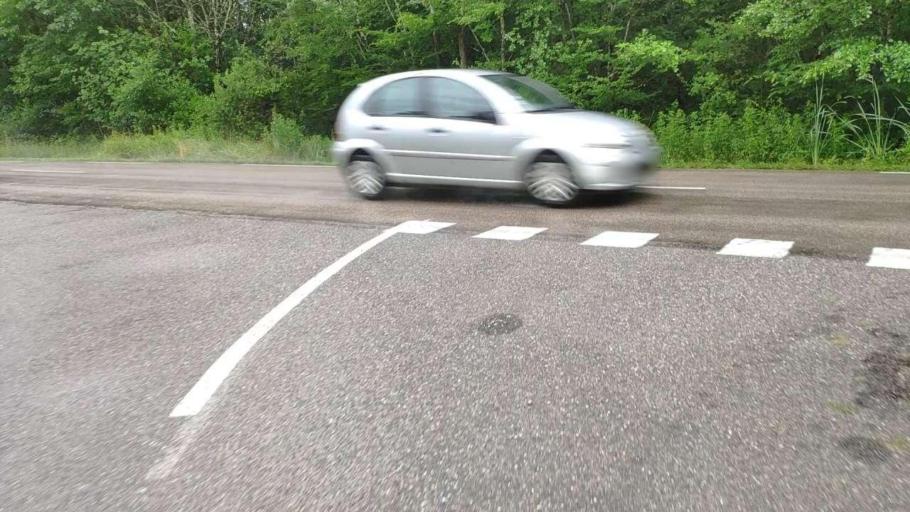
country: FR
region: Franche-Comte
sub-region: Departement du Jura
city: Chaussin
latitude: 46.8909
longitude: 5.4282
